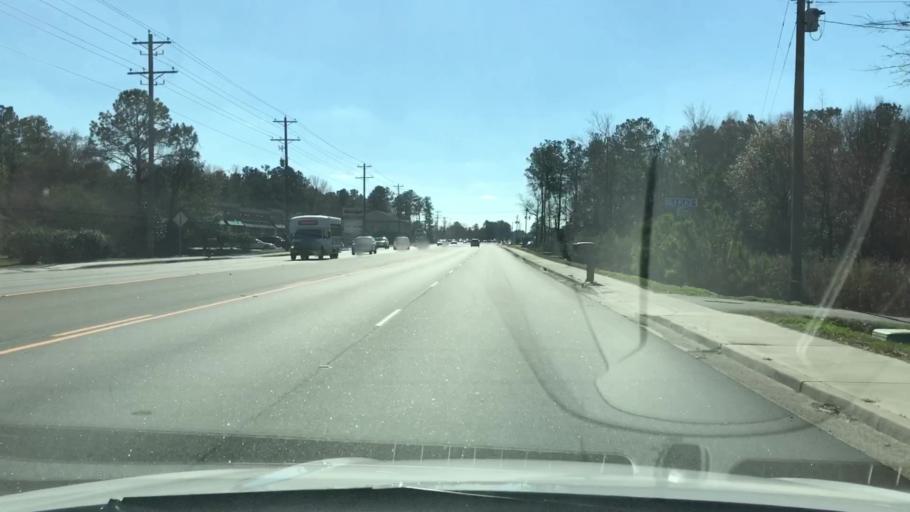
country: US
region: South Carolina
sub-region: Horry County
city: Garden City
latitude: 33.6356
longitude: -79.0334
